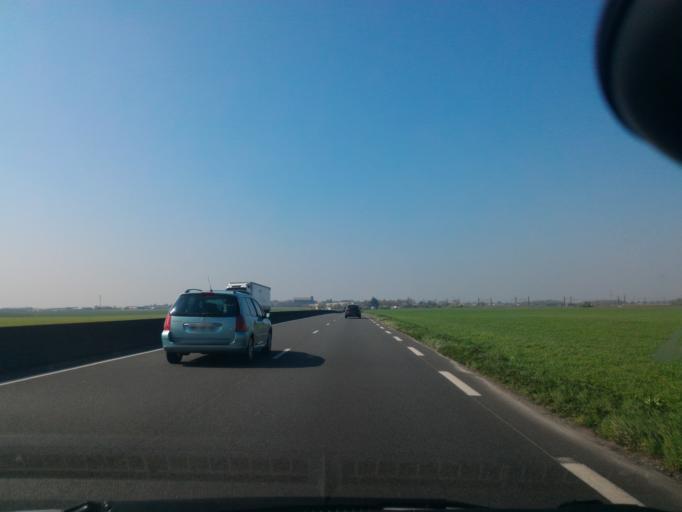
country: FR
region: Ile-de-France
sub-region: Departement de l'Essonne
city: Angerville
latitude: 48.3265
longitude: 2.0199
